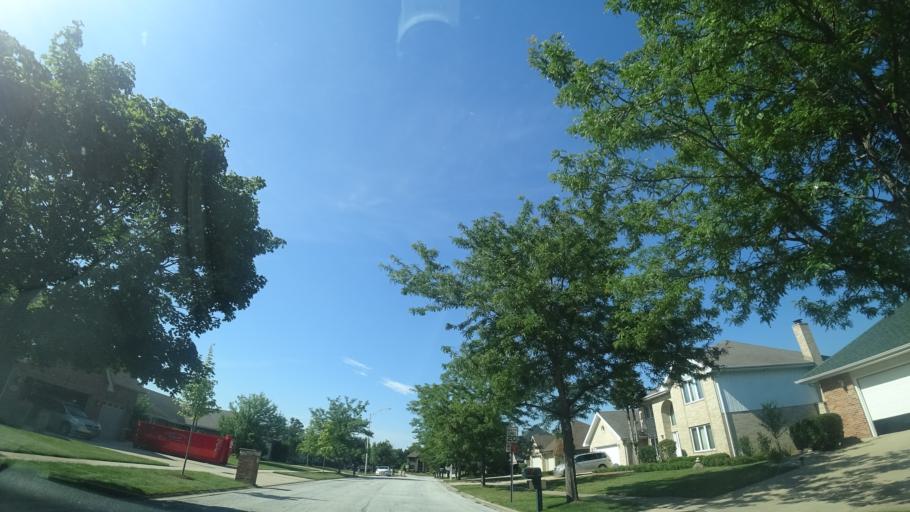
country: US
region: Illinois
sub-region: Will County
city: Mokena
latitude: 41.5689
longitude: -87.8874
